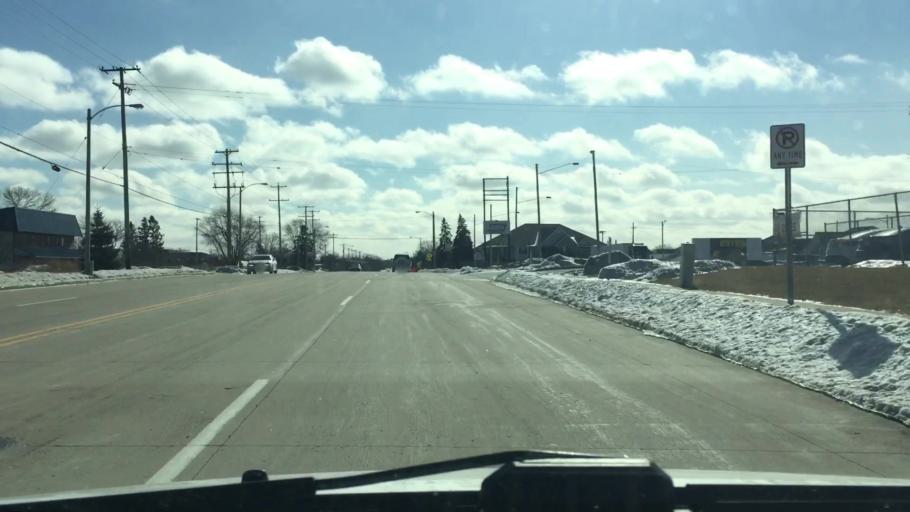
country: US
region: Wisconsin
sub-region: Milwaukee County
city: Greendale
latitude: 42.9224
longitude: -87.9306
